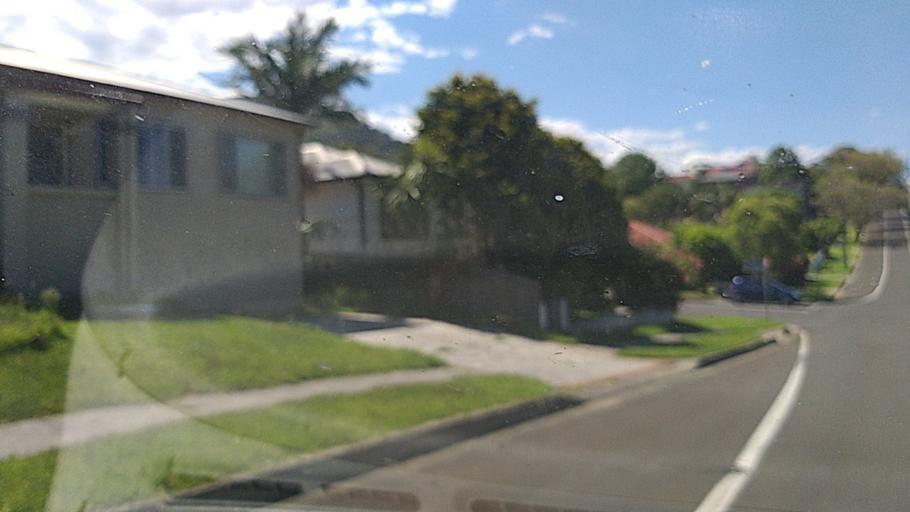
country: AU
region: New South Wales
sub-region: Wollongong
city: Keiraville
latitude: -34.4187
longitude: 150.8695
